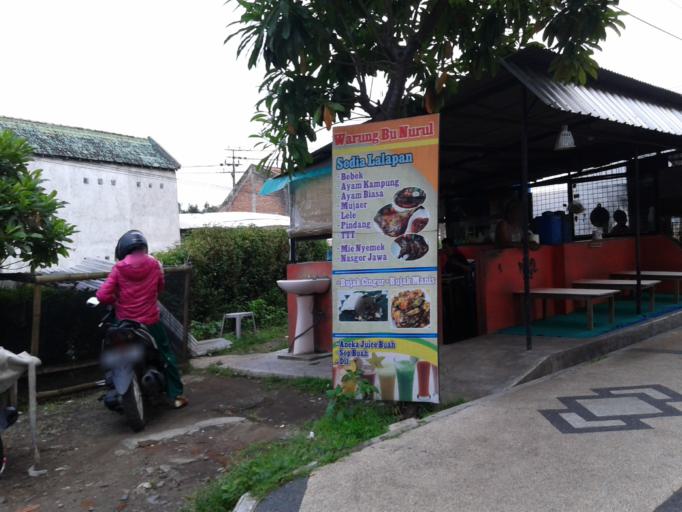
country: ID
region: East Java
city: Singosari
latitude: -7.9335
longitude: 112.6467
